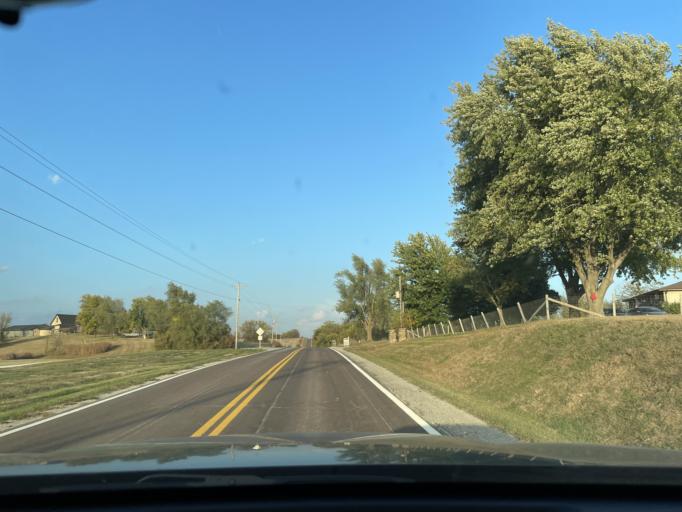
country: US
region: Missouri
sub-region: Andrew County
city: Savannah
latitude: 39.9168
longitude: -94.8742
